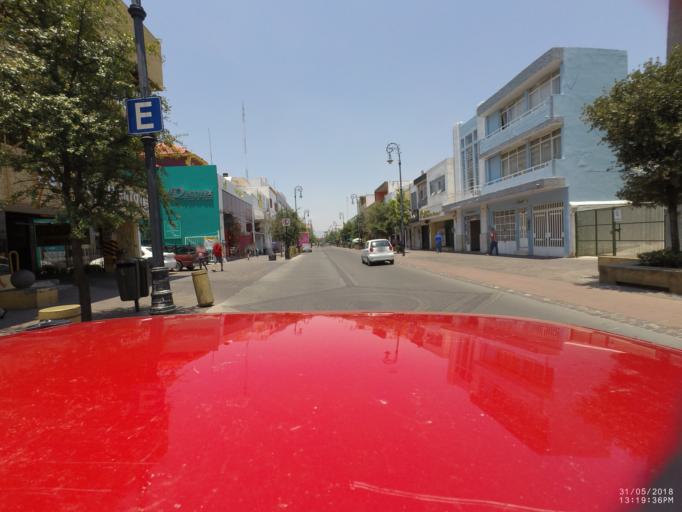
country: MX
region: Aguascalientes
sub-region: Aguascalientes
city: Aguascalientes
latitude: 21.8823
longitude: -102.2914
